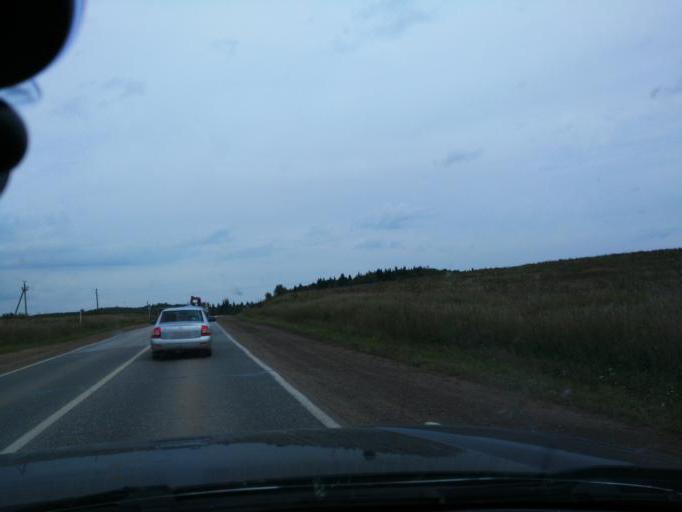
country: RU
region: Perm
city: Chernushka
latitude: 56.5649
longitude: 56.1181
